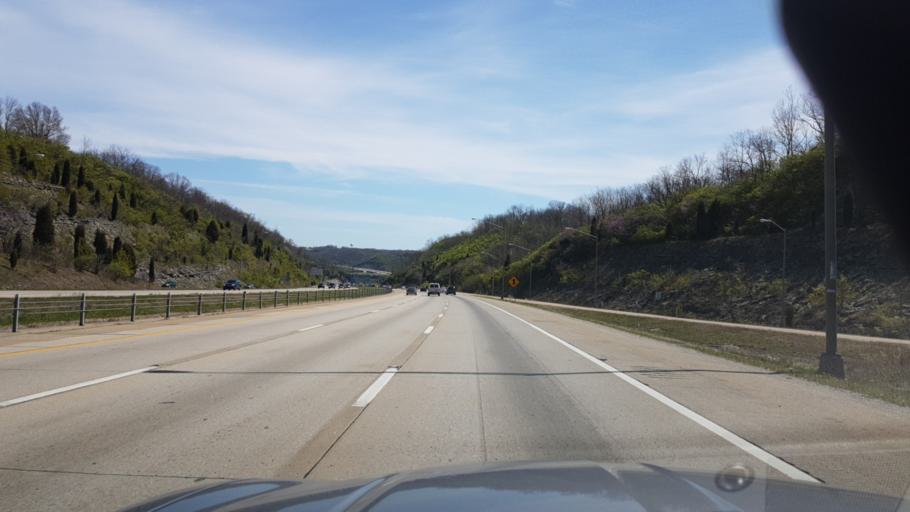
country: US
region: Kentucky
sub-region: Kenton County
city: Taylor Mill
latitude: 39.0219
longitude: -84.5083
